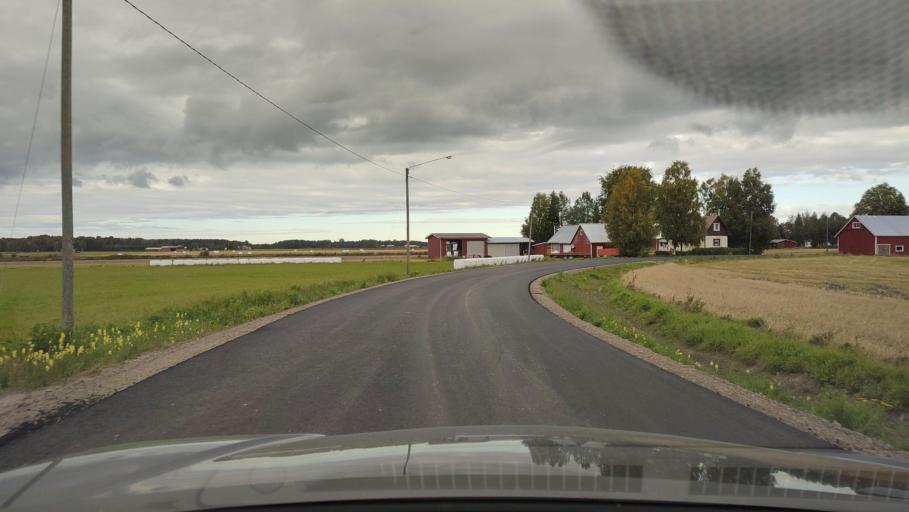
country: FI
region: Southern Ostrobothnia
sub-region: Suupohja
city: Karijoki
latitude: 62.2368
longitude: 21.5695
